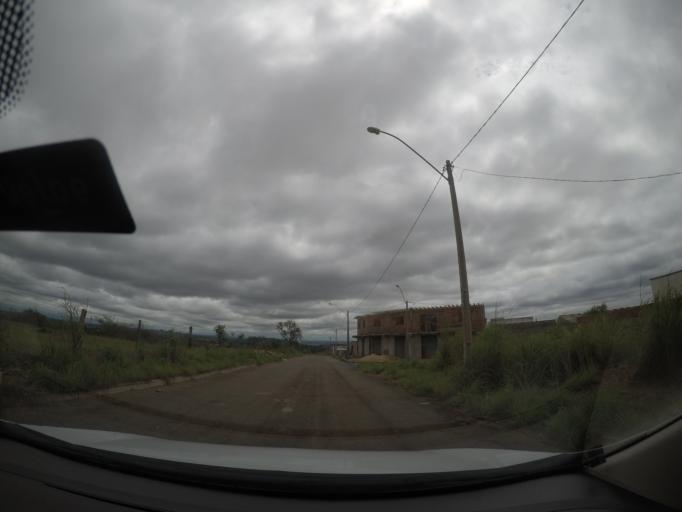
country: BR
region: Goias
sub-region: Trindade
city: Trindade
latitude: -16.7435
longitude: -49.3842
